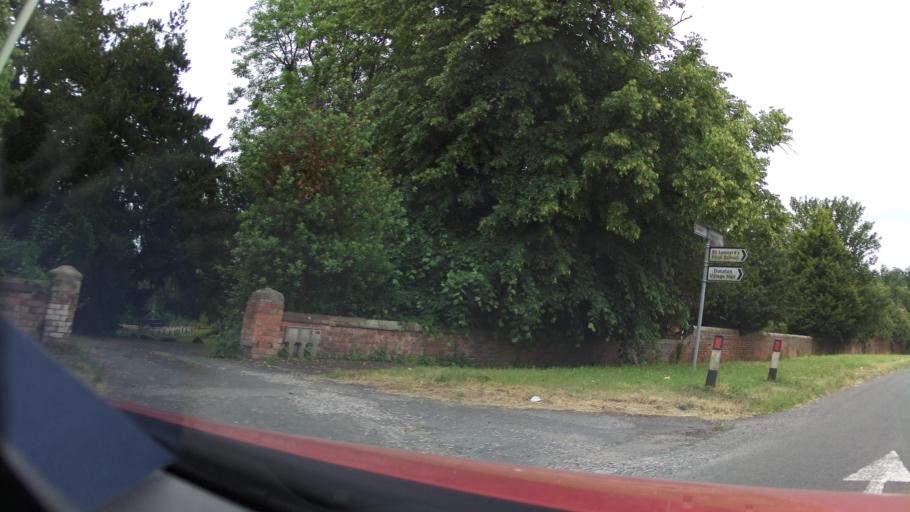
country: GB
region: England
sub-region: Staffordshire
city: Penkridge
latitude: 52.7592
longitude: -2.1084
